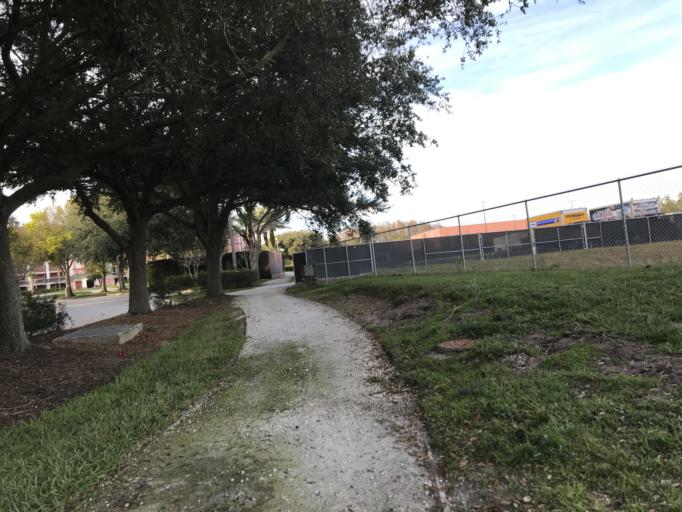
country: US
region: Florida
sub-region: Osceola County
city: Celebration
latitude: 28.3592
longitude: -81.4914
